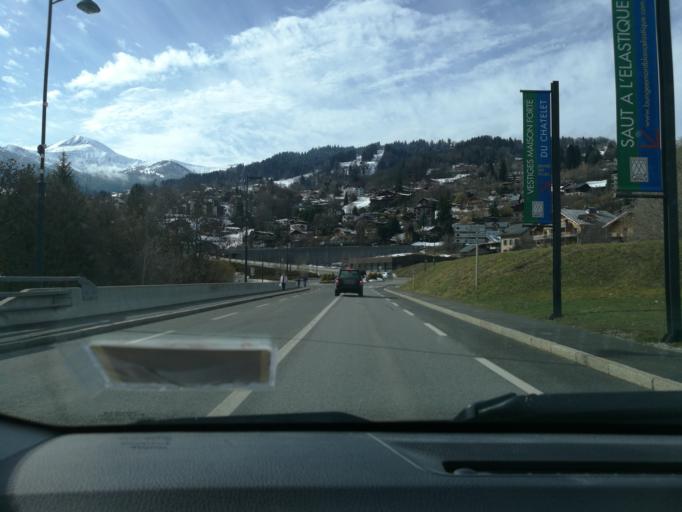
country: FR
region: Rhone-Alpes
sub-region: Departement de la Haute-Savoie
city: Saint-Gervais-les-Bains
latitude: 45.8926
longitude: 6.7085
